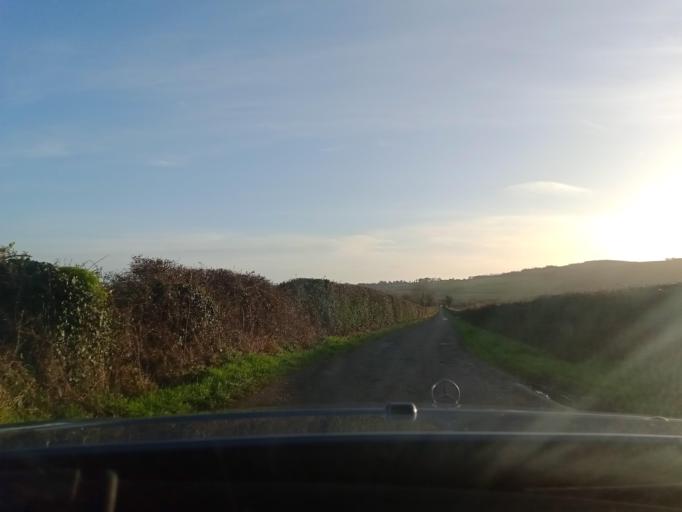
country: IE
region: Leinster
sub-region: Kilkenny
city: Callan
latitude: 52.4788
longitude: -7.4672
